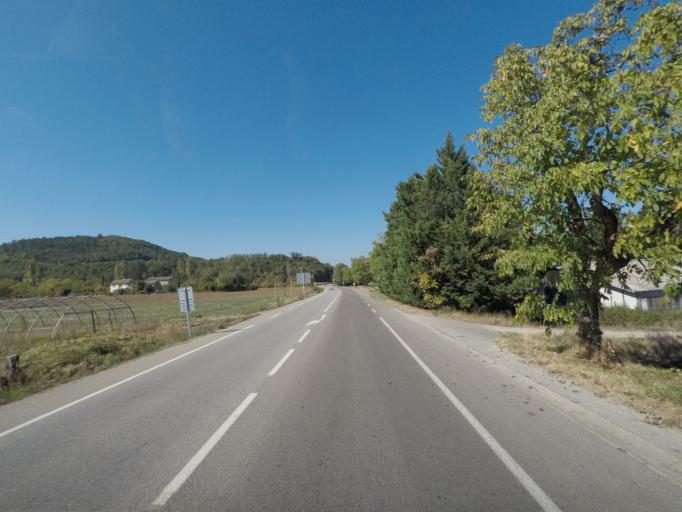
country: FR
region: Rhone-Alpes
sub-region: Departement de la Drome
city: Aouste-sur-Sye
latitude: 44.7055
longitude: 5.0863
